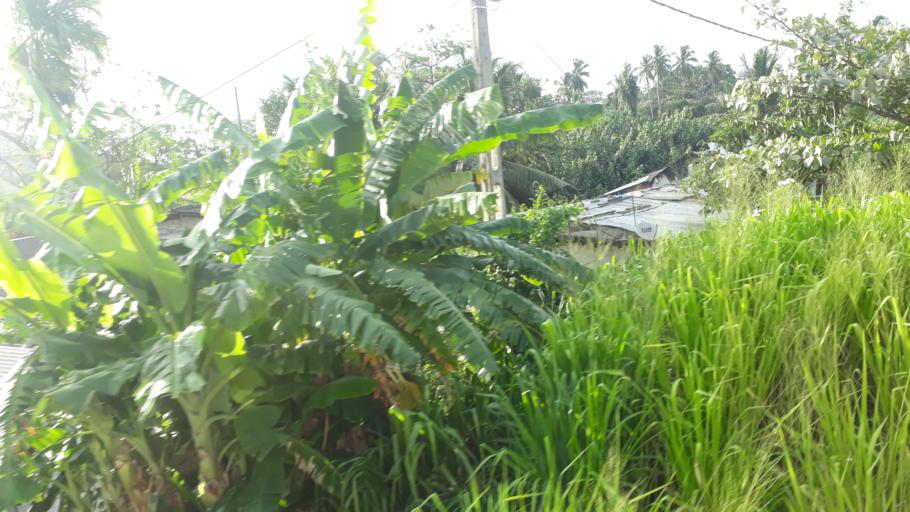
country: LK
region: Western
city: Kolonnawa
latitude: 6.9459
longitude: 79.8859
